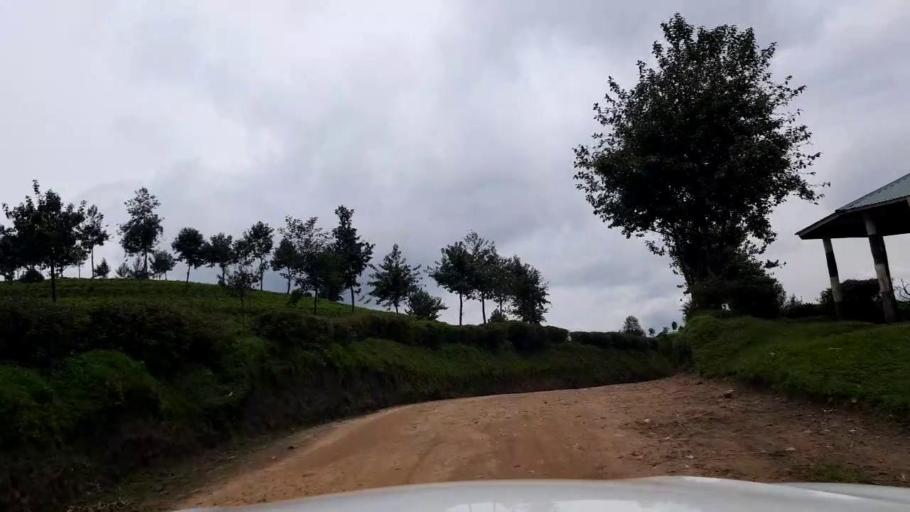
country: RW
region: Western Province
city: Kibuye
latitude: -1.9521
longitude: 29.4117
